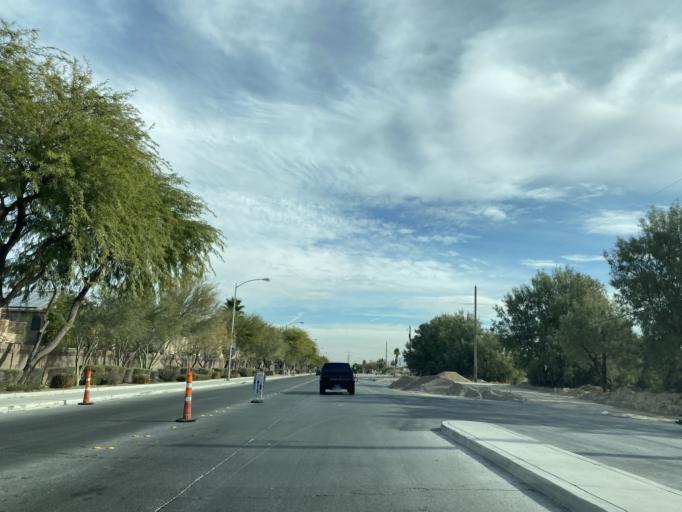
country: US
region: Nevada
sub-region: Clark County
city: North Las Vegas
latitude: 36.2469
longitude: -115.1341
